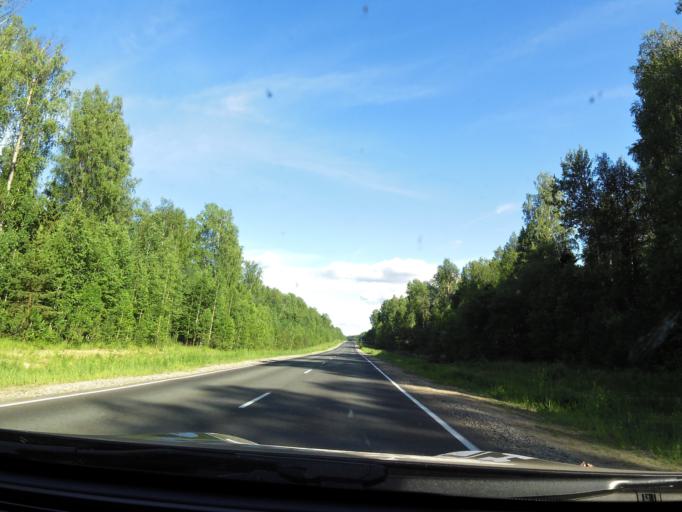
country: RU
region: Kirov
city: Chernaya Kholunitsa
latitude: 58.7860
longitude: 51.8999
